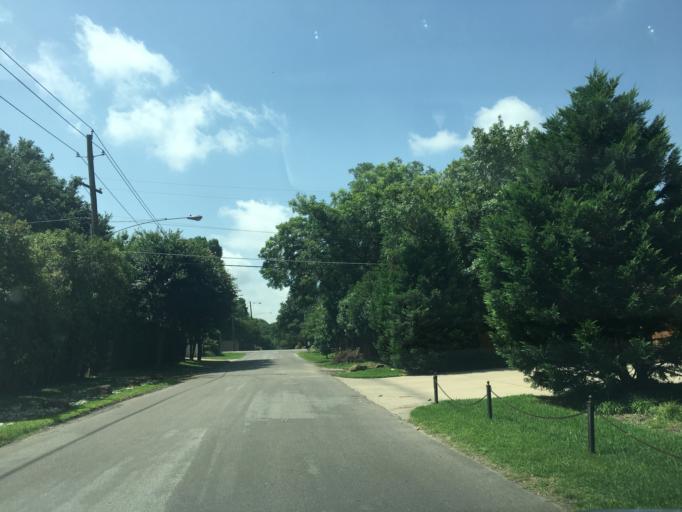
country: US
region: Texas
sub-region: Dallas County
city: University Park
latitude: 32.8881
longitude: -96.7964
